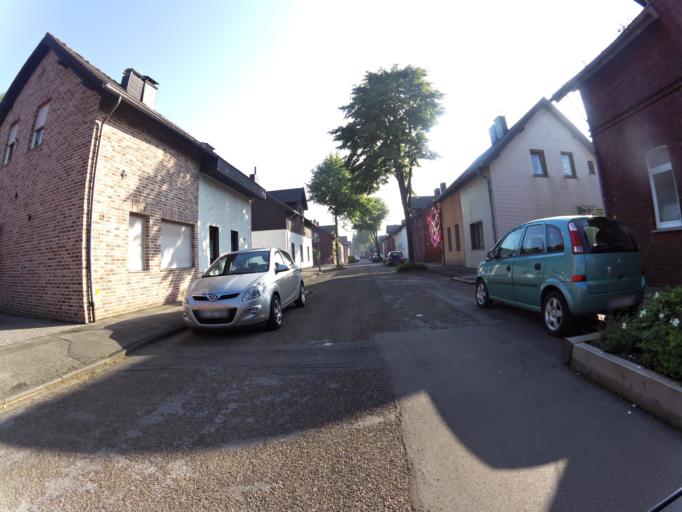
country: DE
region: North Rhine-Westphalia
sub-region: Regierungsbezirk Koln
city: Alsdorf
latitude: 50.8695
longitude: 6.1612
